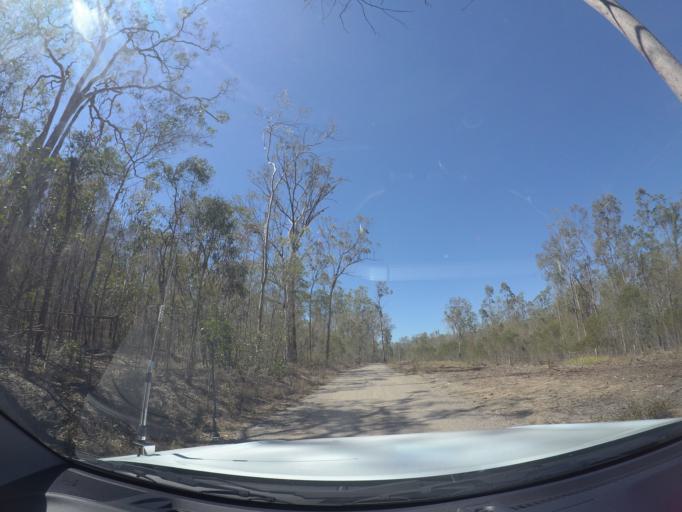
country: AU
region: Queensland
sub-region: Logan
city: North Maclean
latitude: -27.7642
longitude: 152.9399
